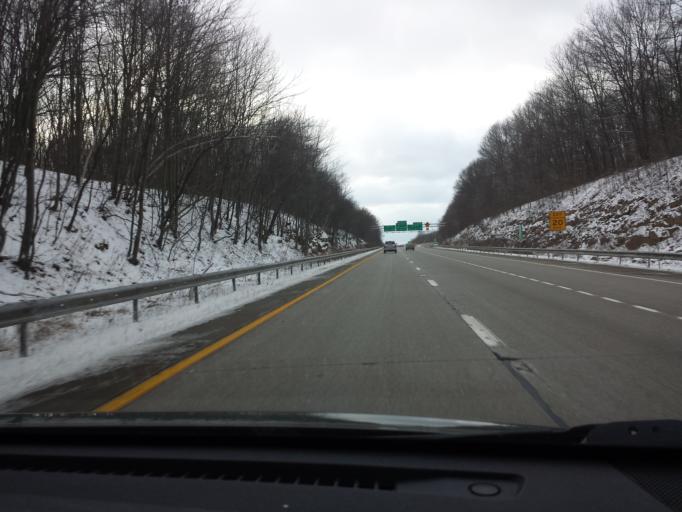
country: US
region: Pennsylvania
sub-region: Luzerne County
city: Harleigh
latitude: 41.0497
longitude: -76.0020
